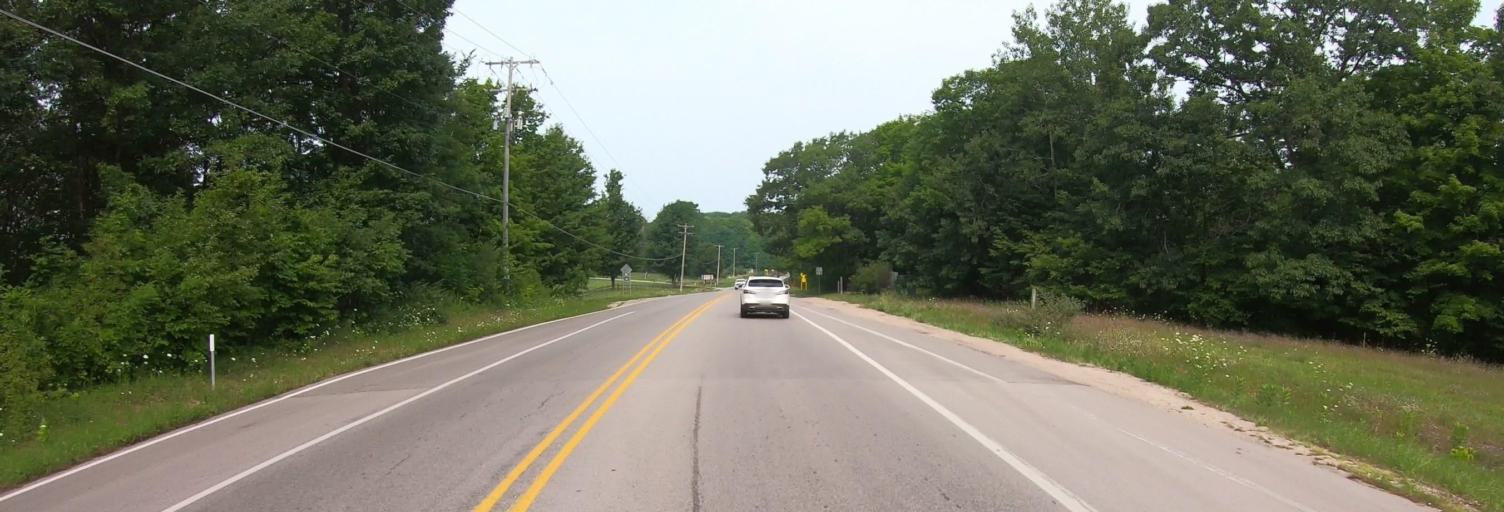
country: US
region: Michigan
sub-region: Leelanau County
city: Leland
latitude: 44.9949
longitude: -85.7698
